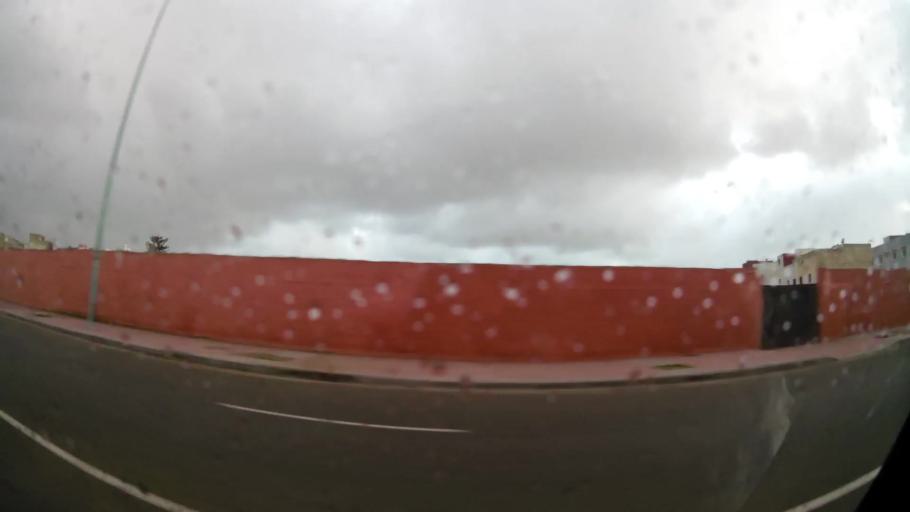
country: MA
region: Doukkala-Abda
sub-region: El-Jadida
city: El Jadida
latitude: 33.2592
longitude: -8.5083
